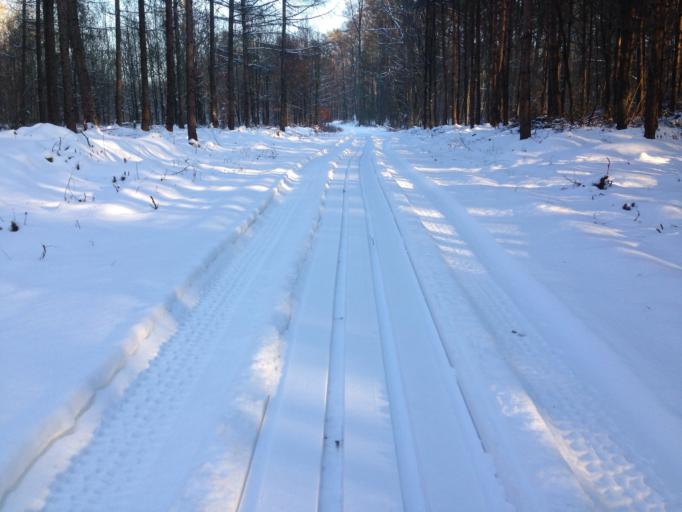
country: PL
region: Kujawsko-Pomorskie
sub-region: Powiat brodnicki
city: Gorzno
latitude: 53.1813
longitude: 19.6834
